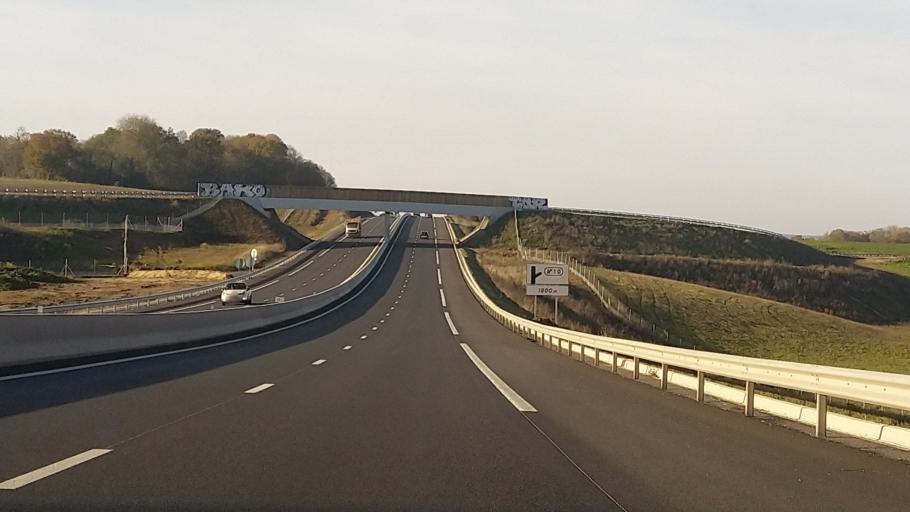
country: FR
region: Ile-de-France
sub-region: Departement du Val-d'Oise
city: Maffliers
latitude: 49.0926
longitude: 2.3038
